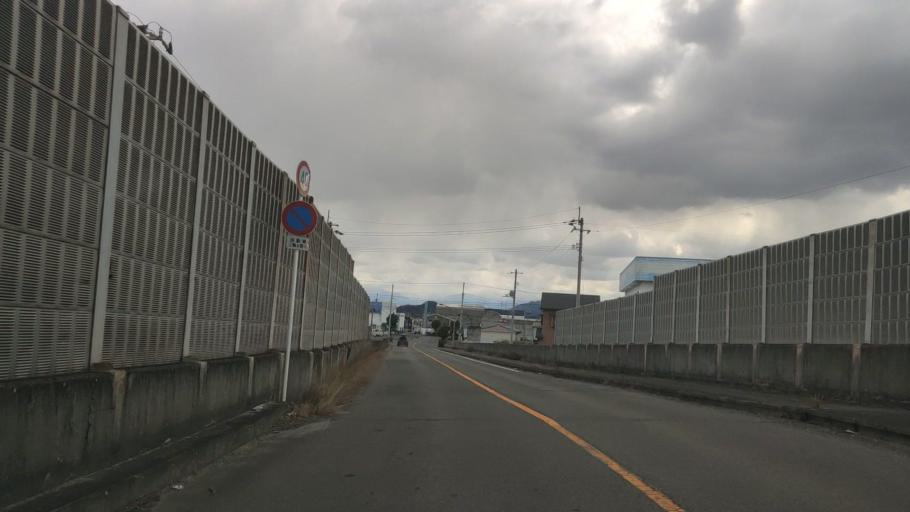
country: JP
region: Ehime
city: Saijo
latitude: 34.0583
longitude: 133.0176
